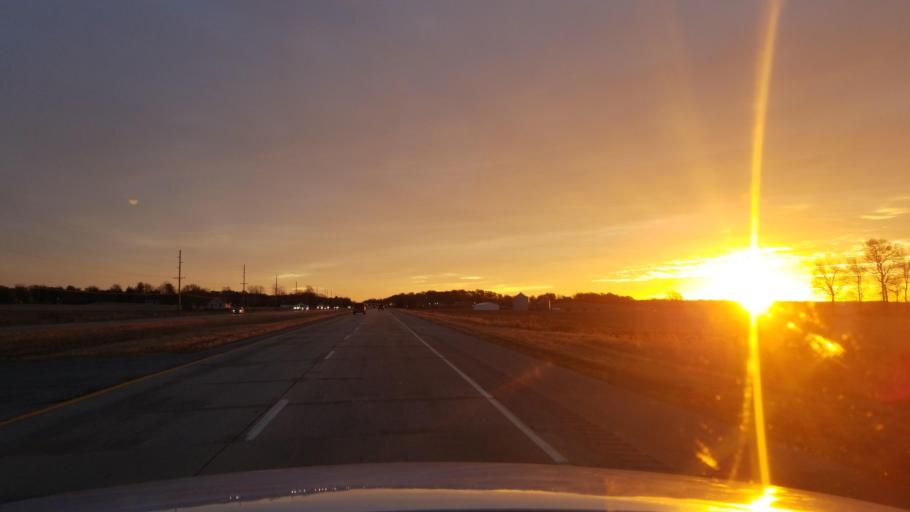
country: US
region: Indiana
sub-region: Posey County
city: Mount Vernon
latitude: 37.9419
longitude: -87.7638
